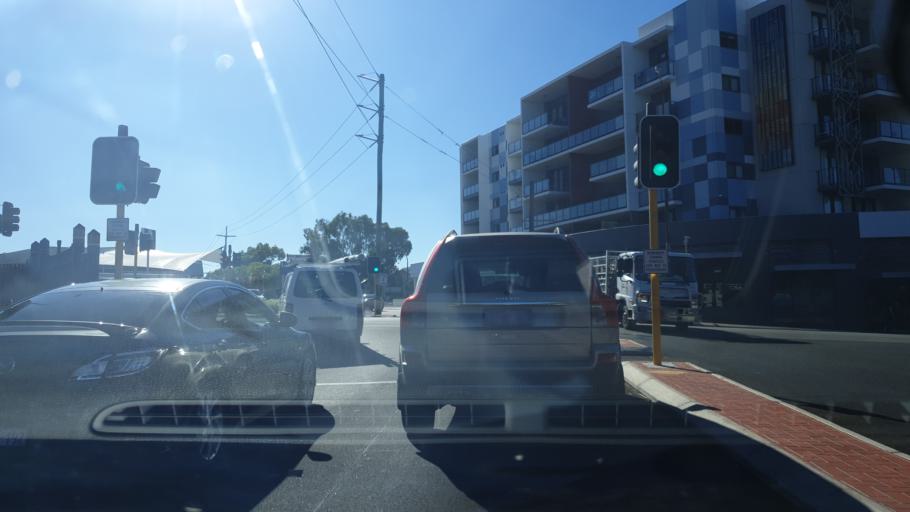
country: AU
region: Western Australia
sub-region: Vincent
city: Mount Lawley
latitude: -31.9450
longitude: 115.8723
